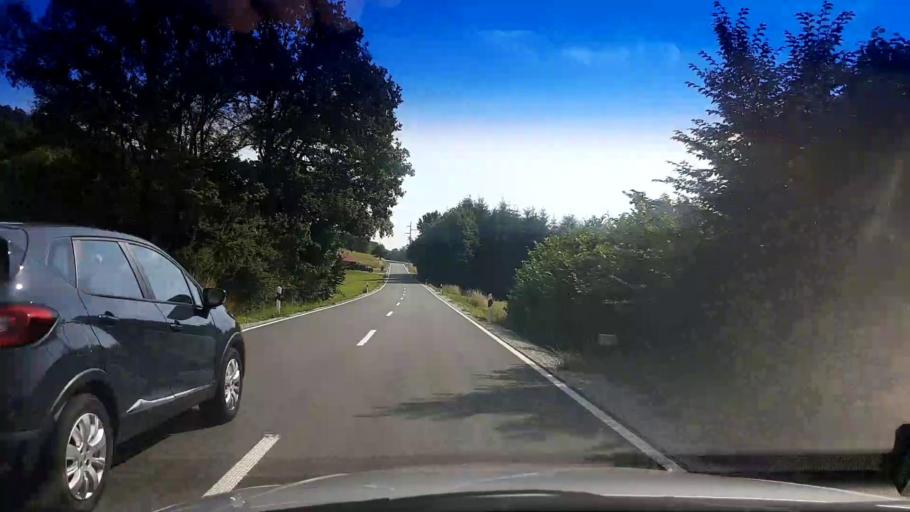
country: DE
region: Bavaria
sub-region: Upper Franconia
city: Mistelgau
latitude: 49.9374
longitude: 11.4247
